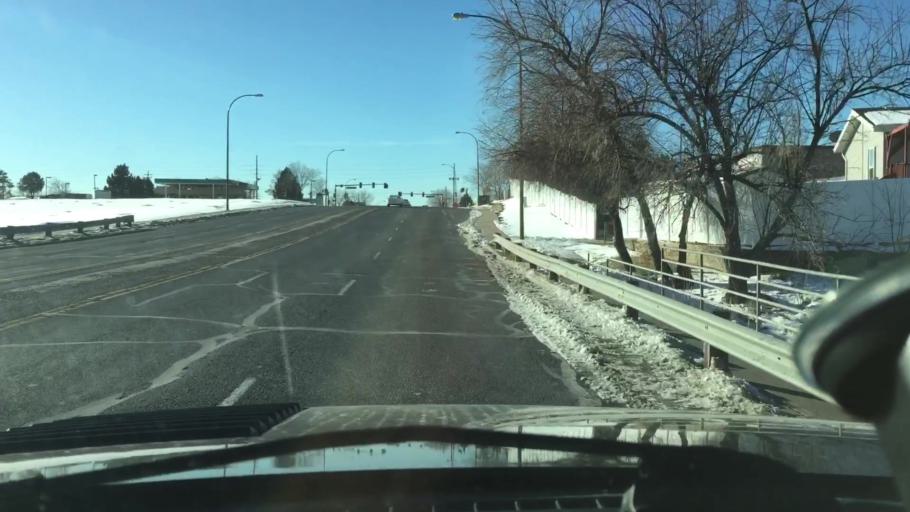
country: US
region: Colorado
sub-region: Adams County
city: Federal Heights
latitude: 39.8657
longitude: -104.9967
